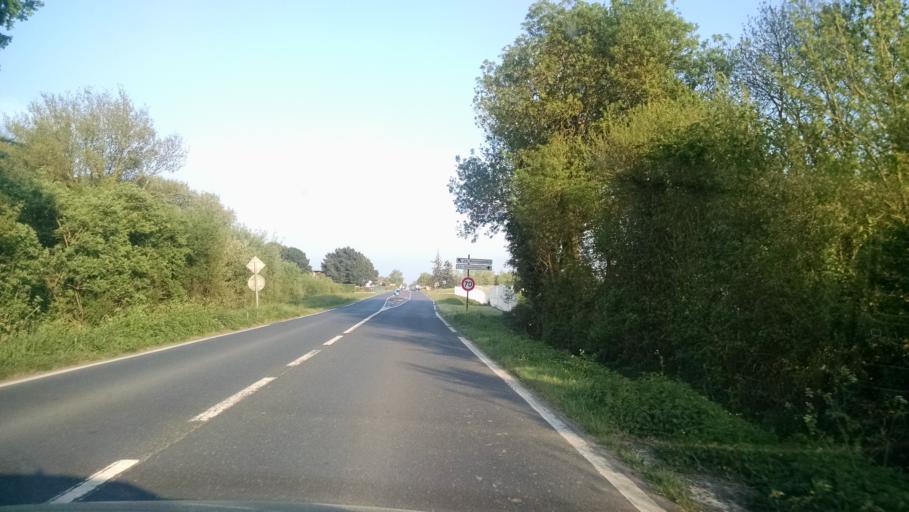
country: FR
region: Pays de la Loire
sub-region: Departement de la Loire-Atlantique
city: Boussay
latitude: 47.0611
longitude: -1.1883
